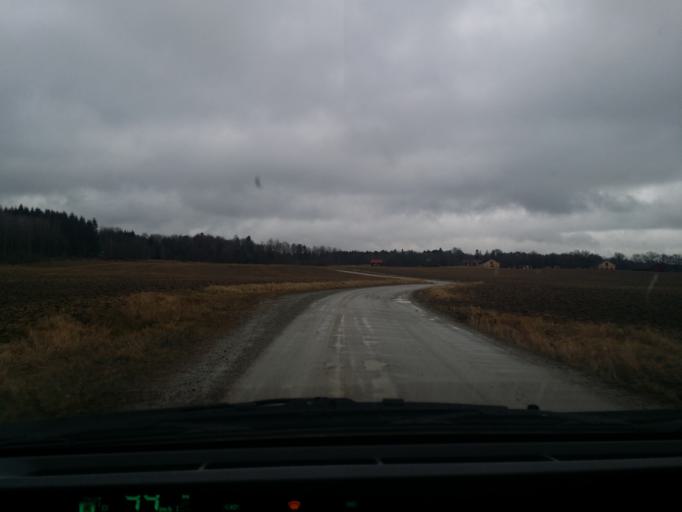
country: SE
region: Vaestmanland
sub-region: Vasteras
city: Skultuna
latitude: 59.7755
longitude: 16.3700
